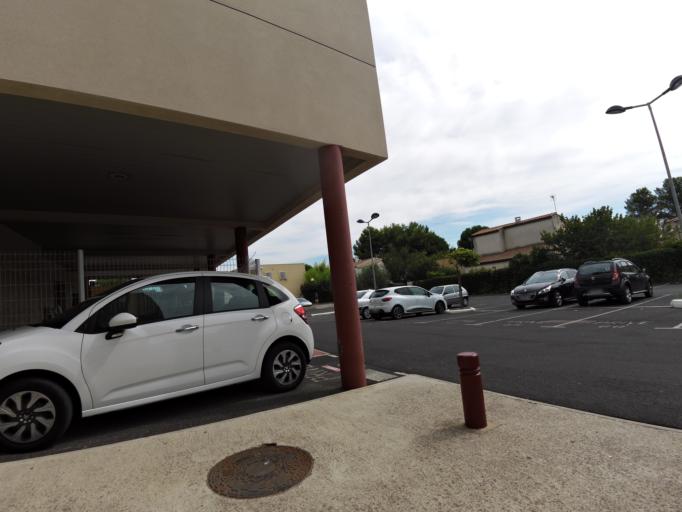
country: FR
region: Languedoc-Roussillon
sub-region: Departement de l'Herault
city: Lunel
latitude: 43.6691
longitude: 4.1283
